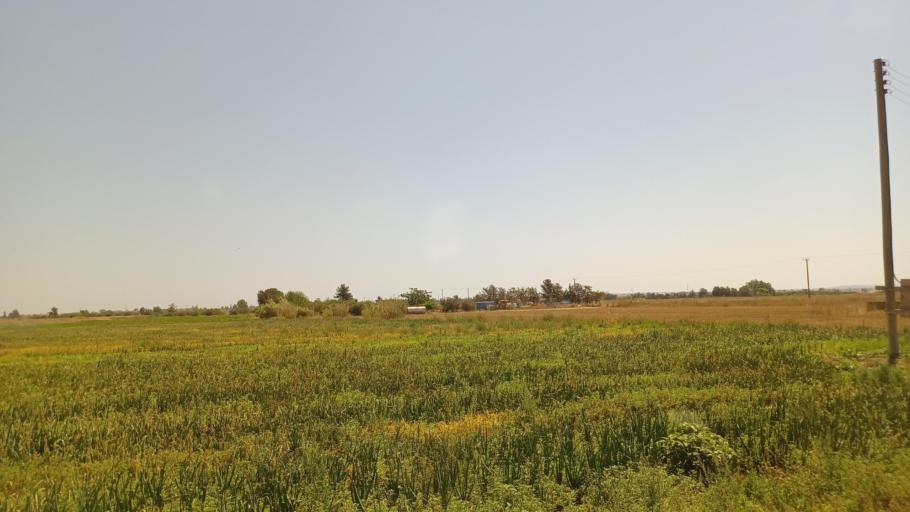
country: CY
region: Ammochostos
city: Avgorou
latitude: 35.0235
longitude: 33.8186
